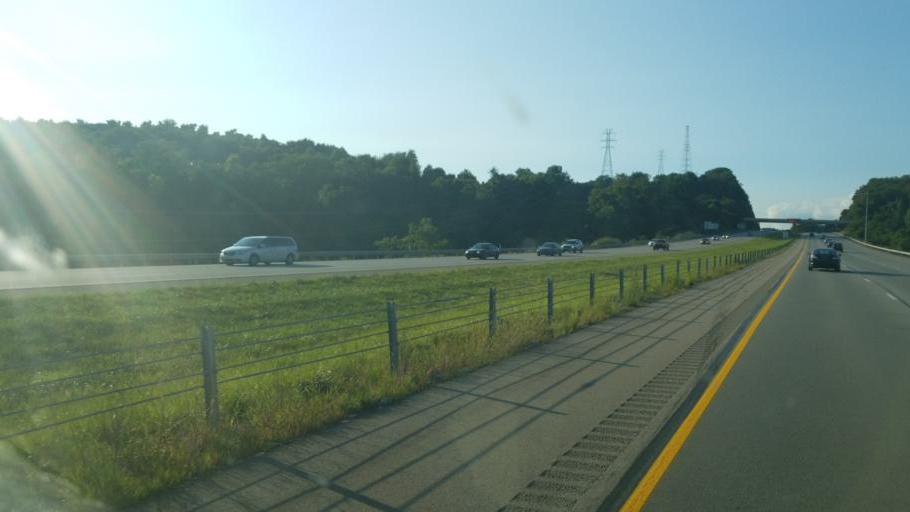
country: US
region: Pennsylvania
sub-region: Allegheny County
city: Heidelberg
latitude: 40.3852
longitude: -80.0970
